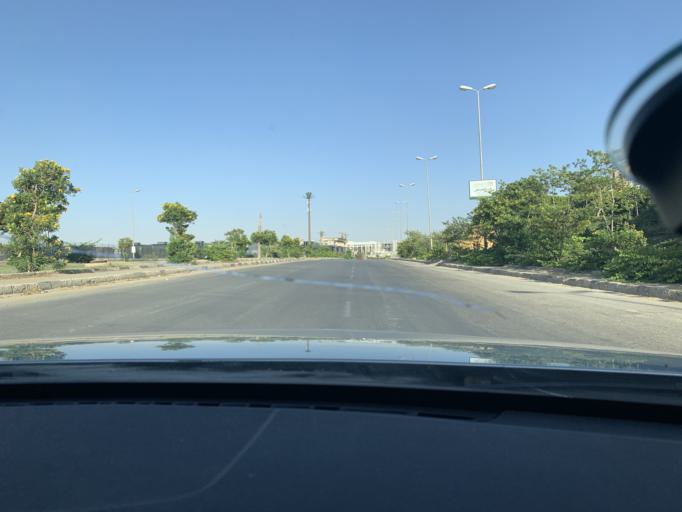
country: EG
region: Muhafazat al Qalyubiyah
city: Al Khankah
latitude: 30.0518
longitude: 31.5085
